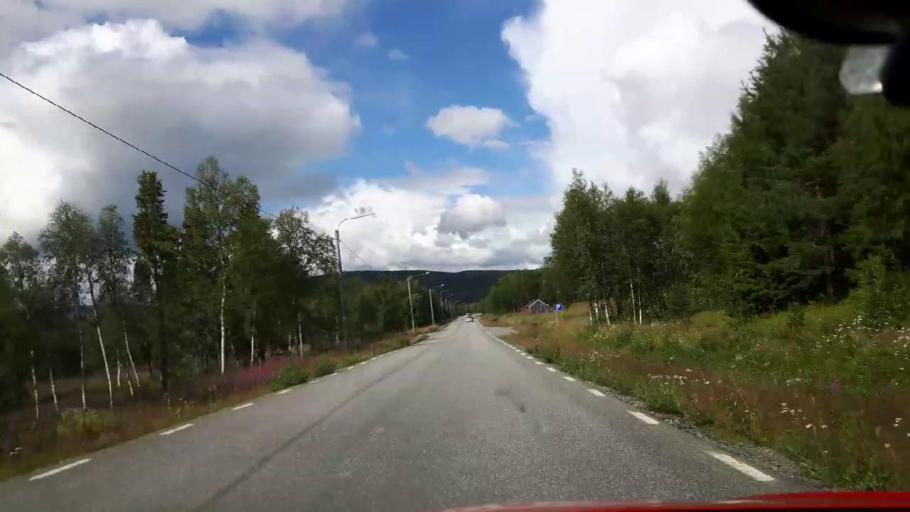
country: NO
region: Nordland
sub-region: Hattfjelldal
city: Hattfjelldal
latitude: 65.0632
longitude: 14.8630
